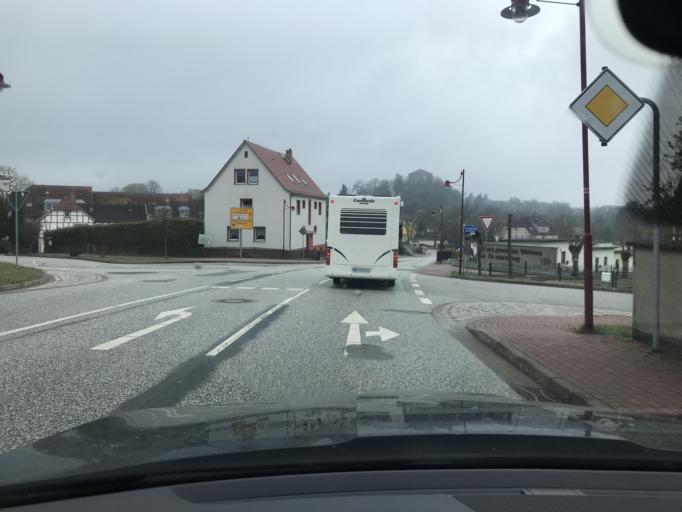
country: DE
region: Saxony-Anhalt
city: Harzgerode
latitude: 51.6454
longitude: 11.1402
